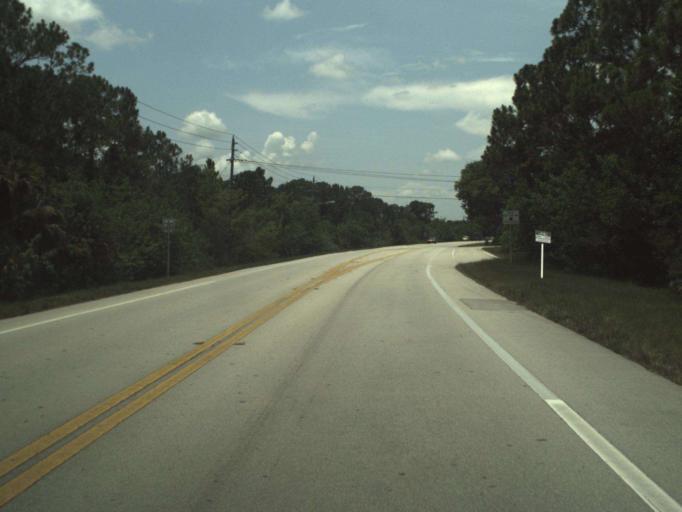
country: US
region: Florida
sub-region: Saint Lucie County
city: Lakewood Park
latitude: 27.5435
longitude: -80.3771
